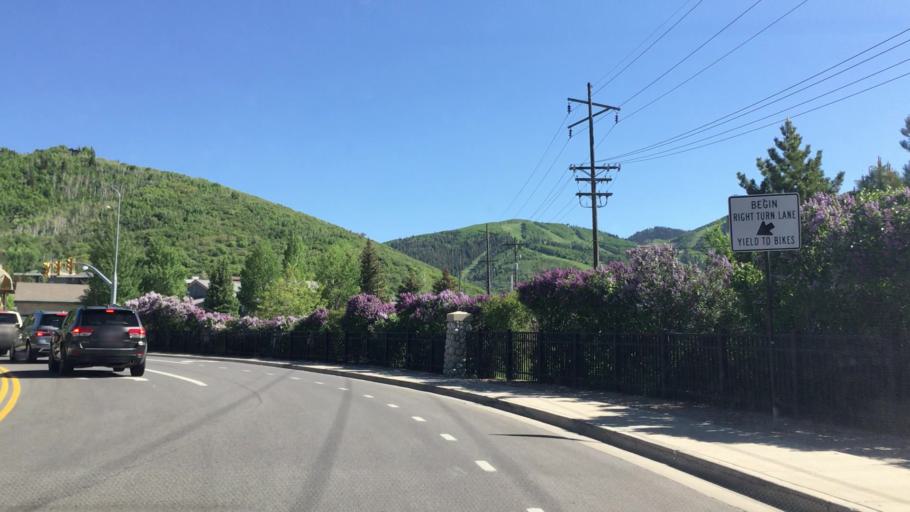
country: US
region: Utah
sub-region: Summit County
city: Park City
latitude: 40.6636
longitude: -111.5014
